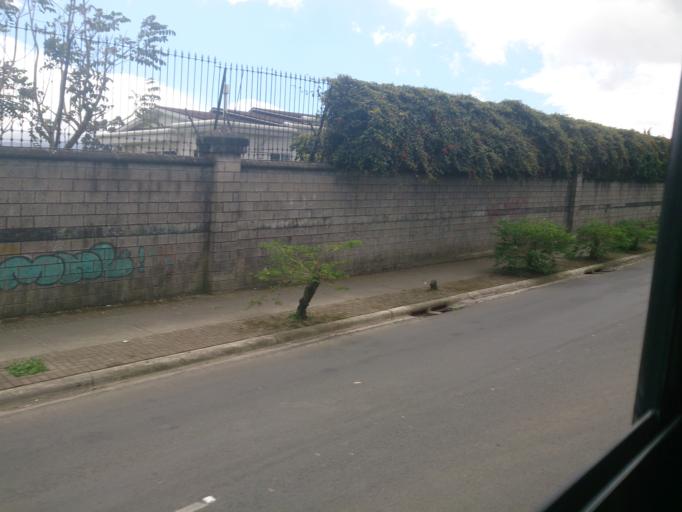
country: CR
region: Cartago
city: Concepcion
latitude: 9.9295
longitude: -84.0073
